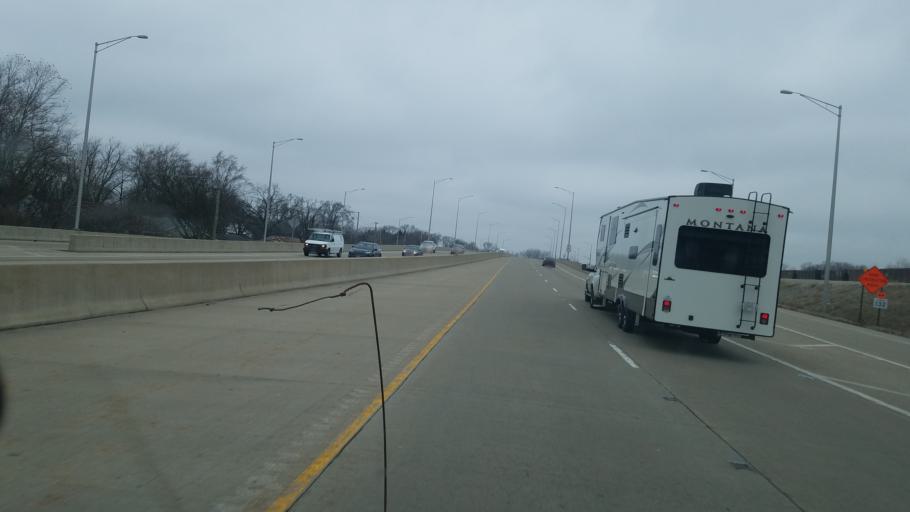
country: US
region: Illinois
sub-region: Lake County
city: Gurnee
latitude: 42.3683
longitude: -87.8952
